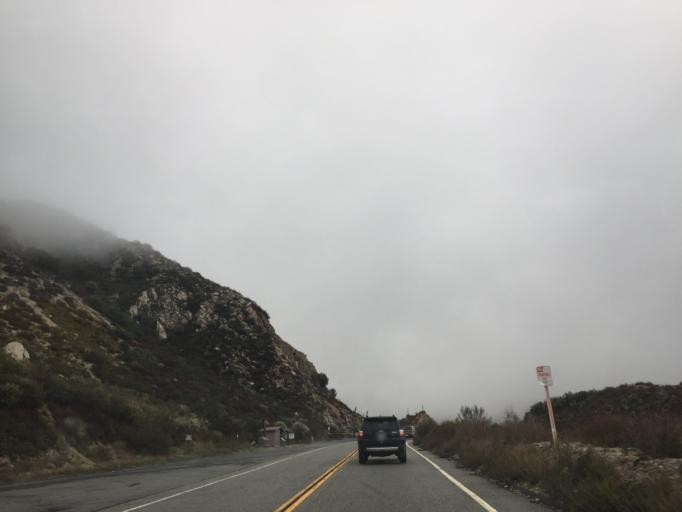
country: US
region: California
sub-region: Los Angeles County
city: Glendora
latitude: 34.2868
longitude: -117.8435
